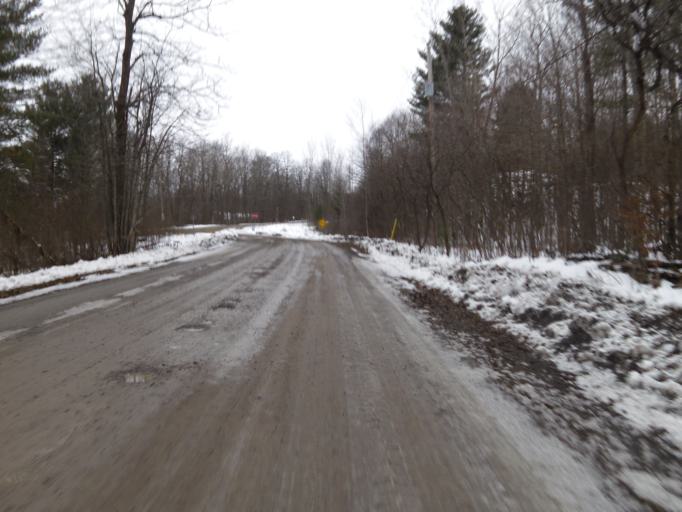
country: CA
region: Ontario
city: Carleton Place
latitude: 45.1594
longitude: -76.2402
